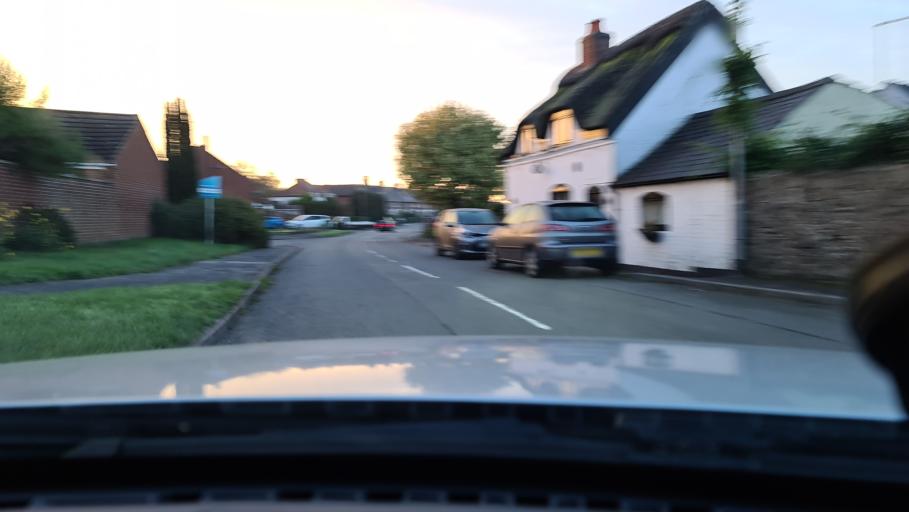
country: GB
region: England
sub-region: Leicestershire
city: Sapcote
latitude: 52.5353
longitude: -1.2786
